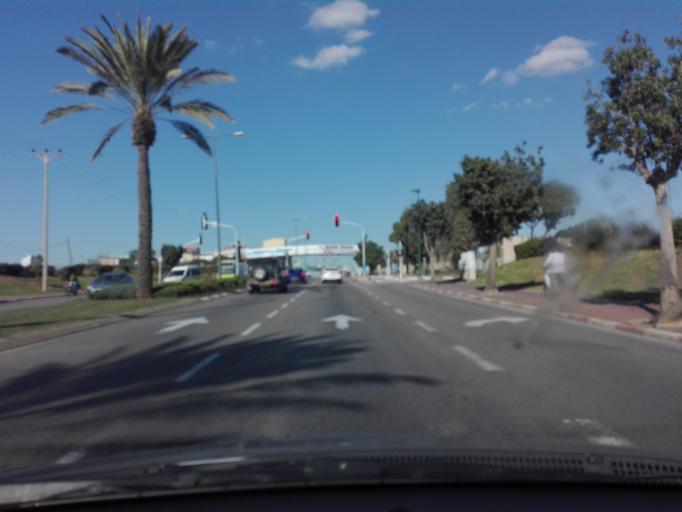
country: IL
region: Central District
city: Netanya
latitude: 32.3081
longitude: 34.8549
